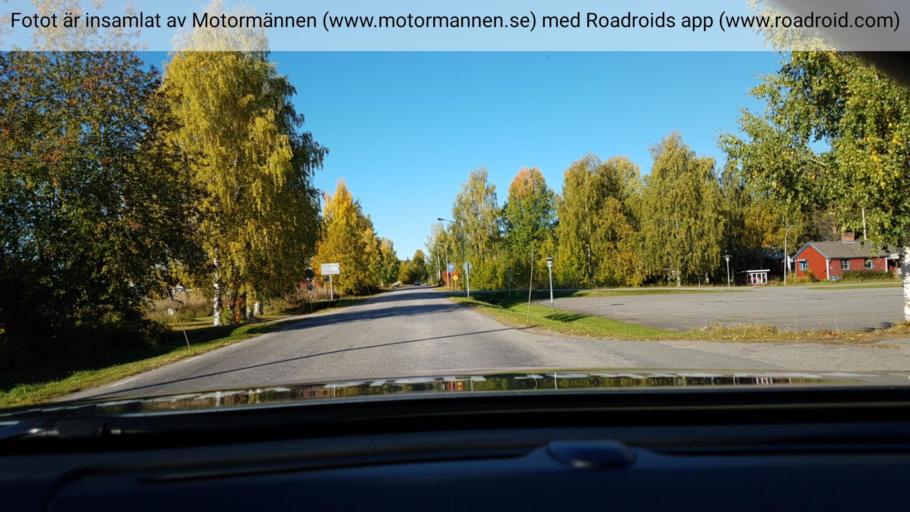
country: SE
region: Norrbotten
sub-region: Gallivare Kommun
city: Gaellivare
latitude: 66.4289
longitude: 20.6242
